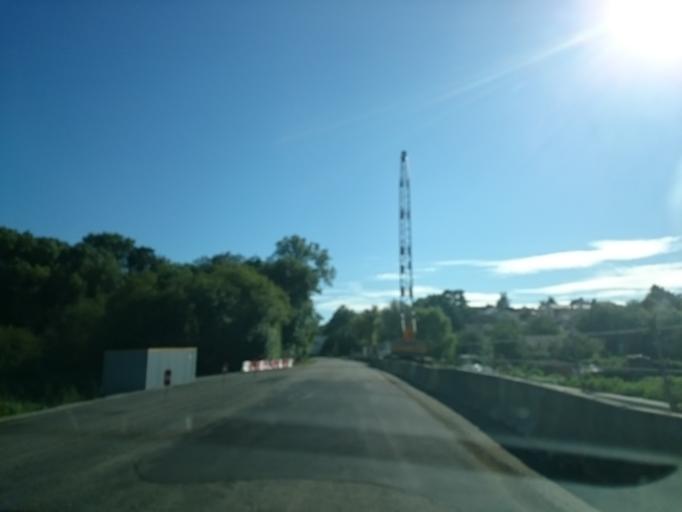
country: FR
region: Pays de la Loire
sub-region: Departement de la Loire-Atlantique
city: La Montagne
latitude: 47.1954
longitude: -1.6925
